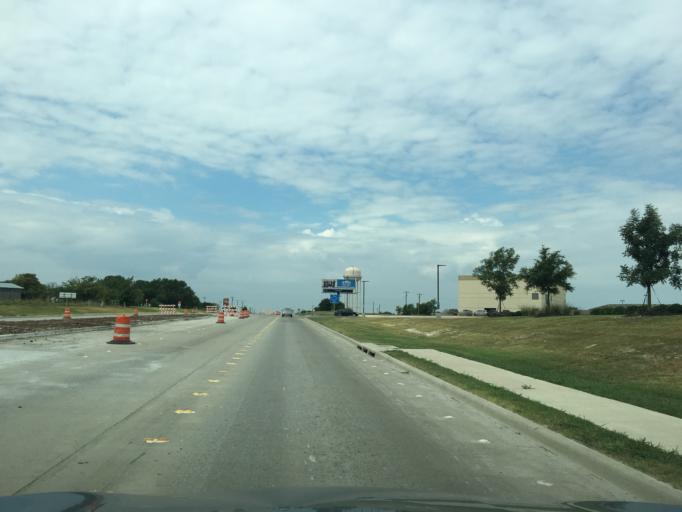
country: US
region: Texas
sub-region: Collin County
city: Melissa
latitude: 33.2818
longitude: -96.5642
